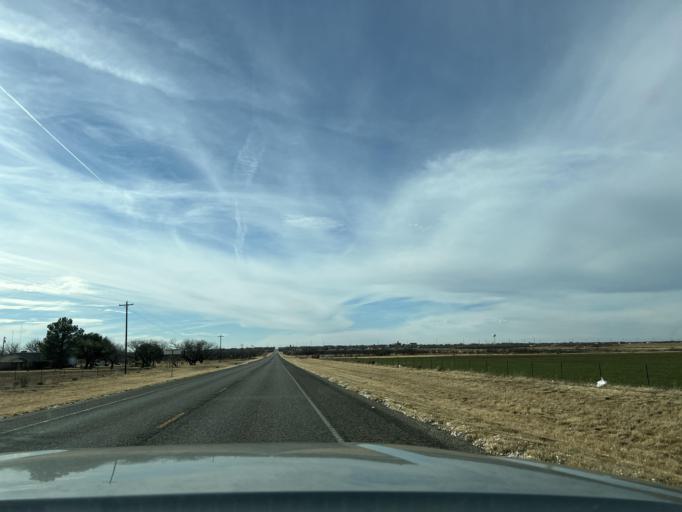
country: US
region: Texas
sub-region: Jones County
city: Anson
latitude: 32.7514
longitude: -99.8720
